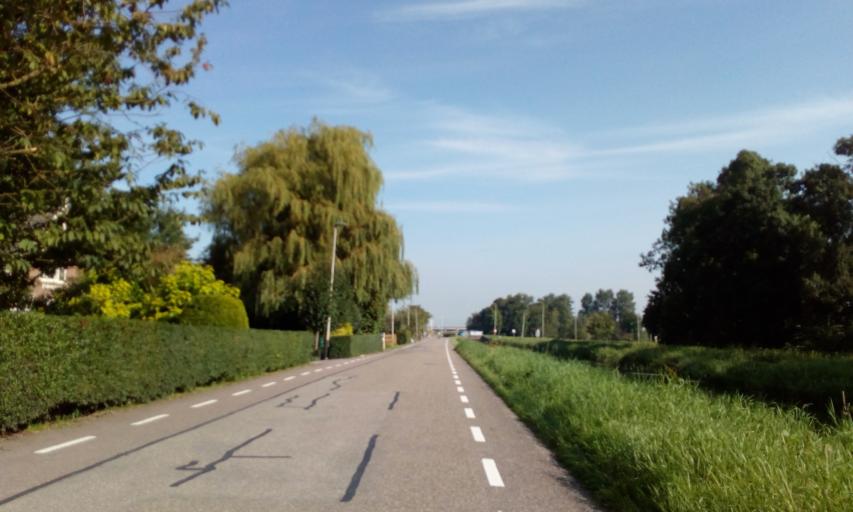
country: NL
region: South Holland
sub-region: Gemeente Lansingerland
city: Bleiswijk
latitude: 52.0226
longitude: 4.5797
